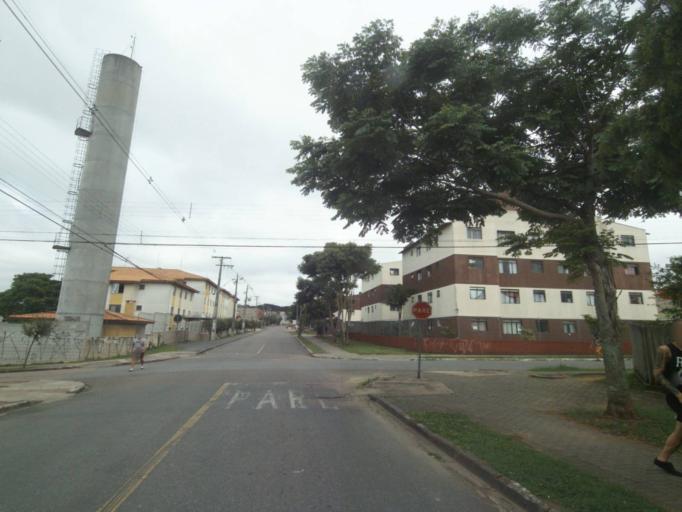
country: BR
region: Parana
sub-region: Sao Jose Dos Pinhais
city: Sao Jose dos Pinhais
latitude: -25.5515
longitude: -49.2666
